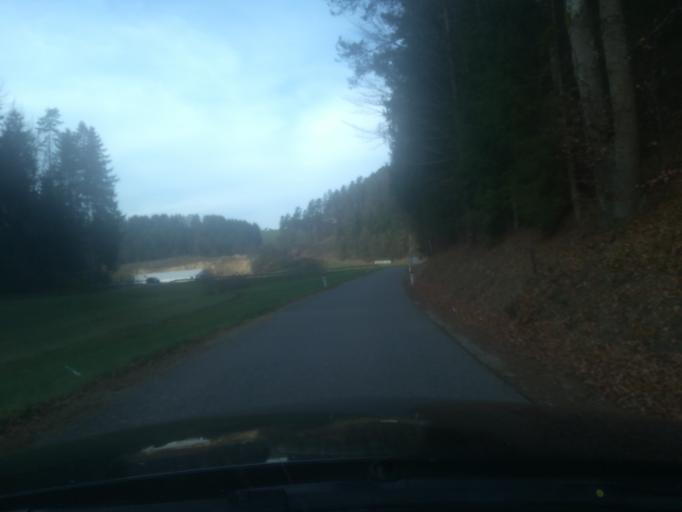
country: AT
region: Upper Austria
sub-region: Politischer Bezirk Perg
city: Perg
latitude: 48.3382
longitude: 14.6450
